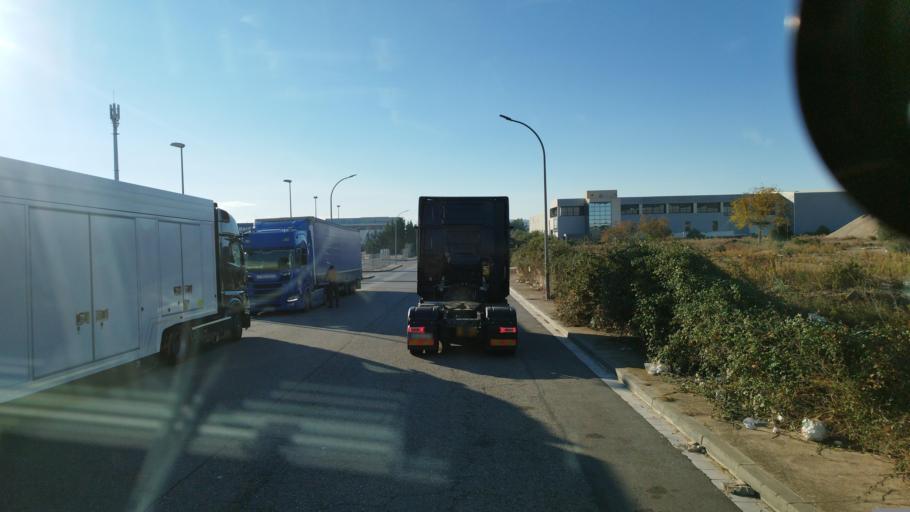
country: ES
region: Catalonia
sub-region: Provincia de Tarragona
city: la Bisbal del Penedes
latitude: 41.2717
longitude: 1.5167
